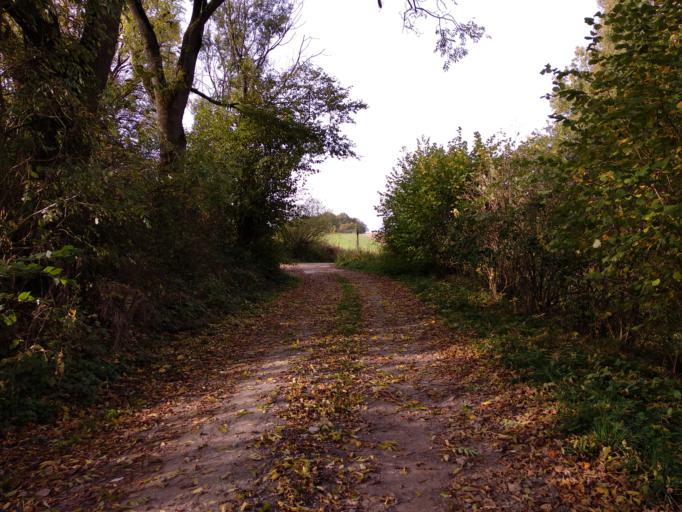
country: DE
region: North Rhine-Westphalia
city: Beverungen
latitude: 51.6866
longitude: 9.3512
